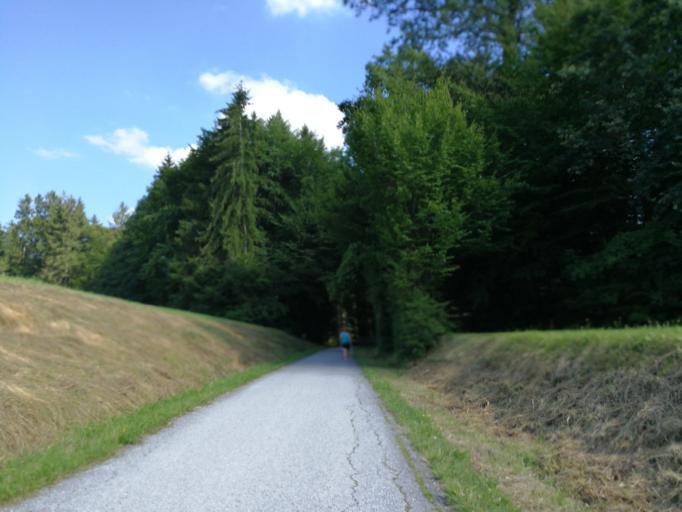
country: AT
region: Salzburg
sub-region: Politischer Bezirk Salzburg-Umgebung
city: Hallwang
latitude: 47.8467
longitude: 13.0868
